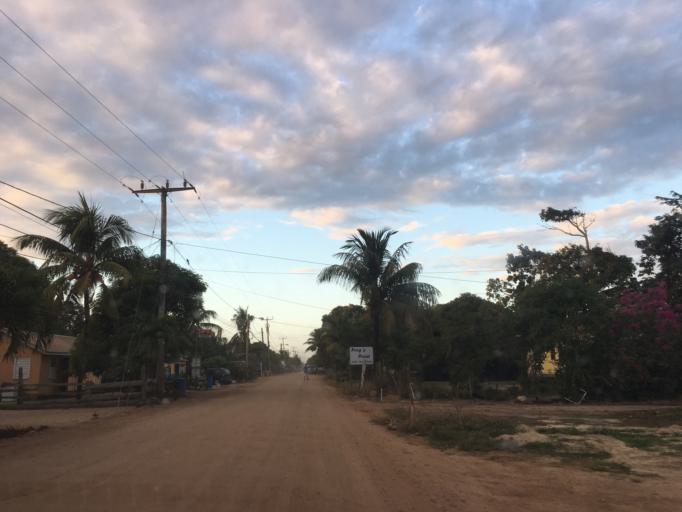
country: BZ
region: Stann Creek
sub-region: Dangriga
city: Dangriga
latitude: 16.8516
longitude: -88.2795
